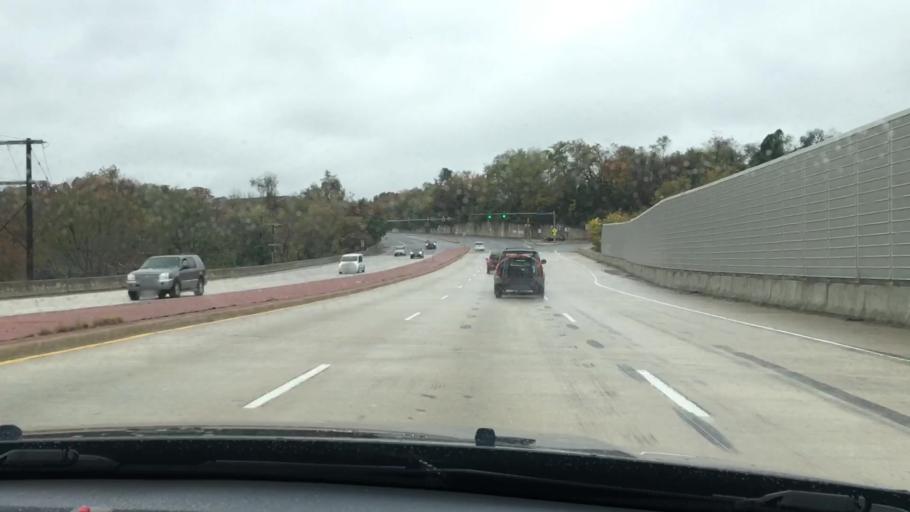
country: US
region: Virginia
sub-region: Prince William County
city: Woodbridge
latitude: 38.6830
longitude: -77.2584
